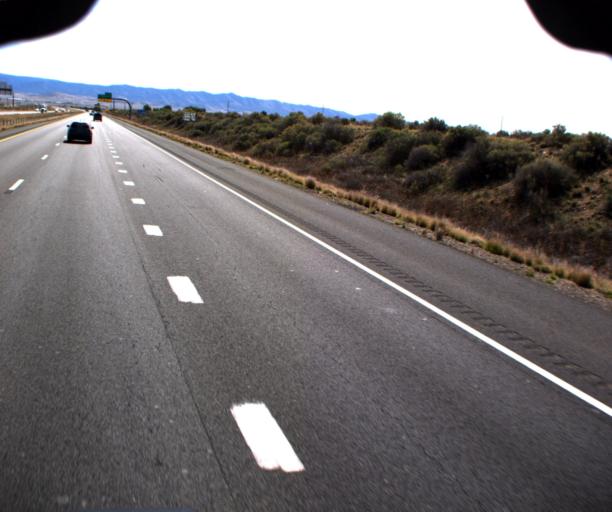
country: US
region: Arizona
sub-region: Yavapai County
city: Prescott Valley
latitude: 34.6337
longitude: -112.3474
